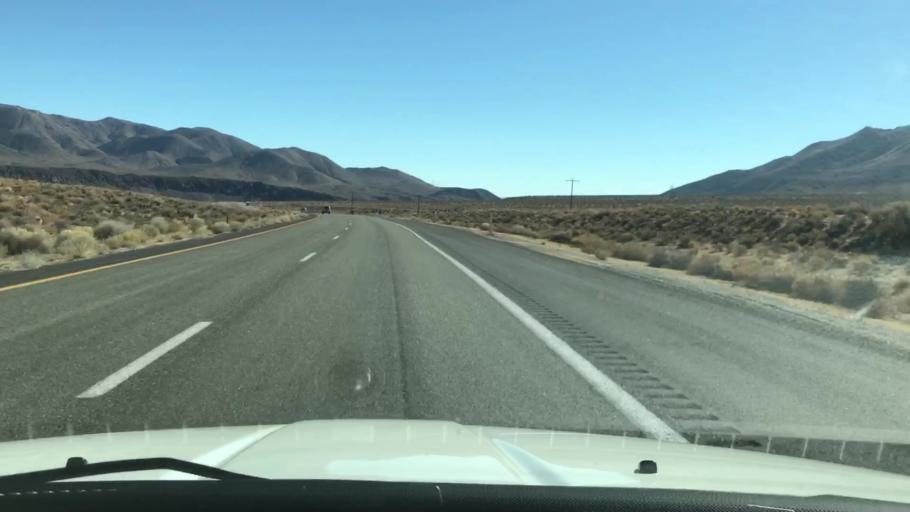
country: US
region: California
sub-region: Kern County
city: Inyokern
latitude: 35.9661
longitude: -117.9194
